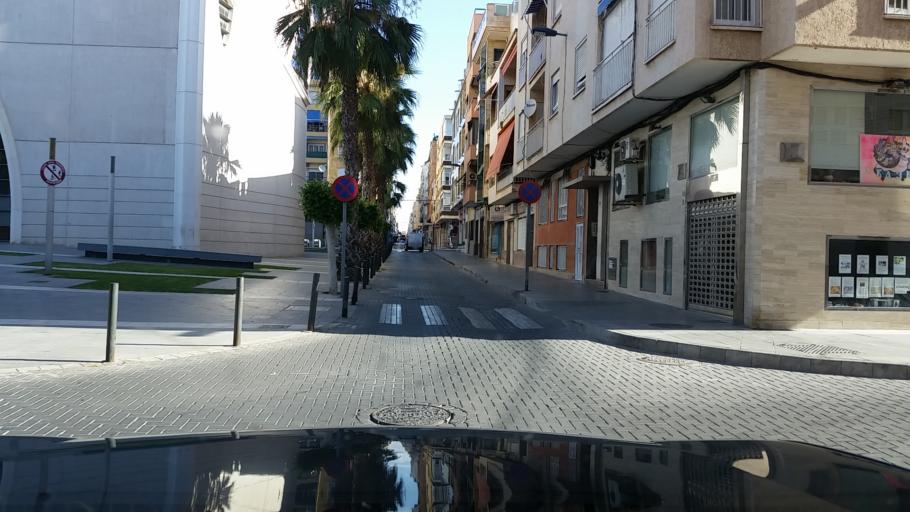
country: ES
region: Valencia
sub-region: Provincia de Alicante
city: Torrevieja
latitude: 37.9761
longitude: -0.6762
